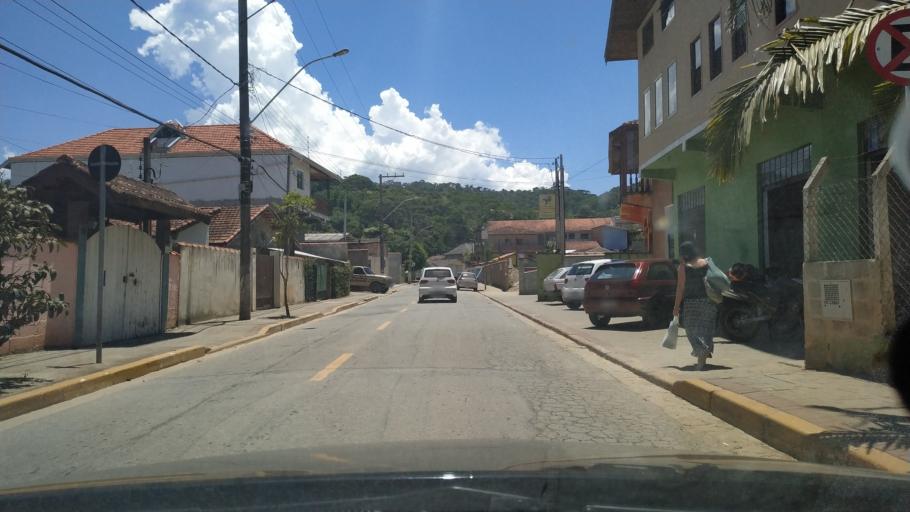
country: BR
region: Sao Paulo
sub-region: Campos Do Jordao
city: Campos do Jordao
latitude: -22.8224
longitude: -45.6749
